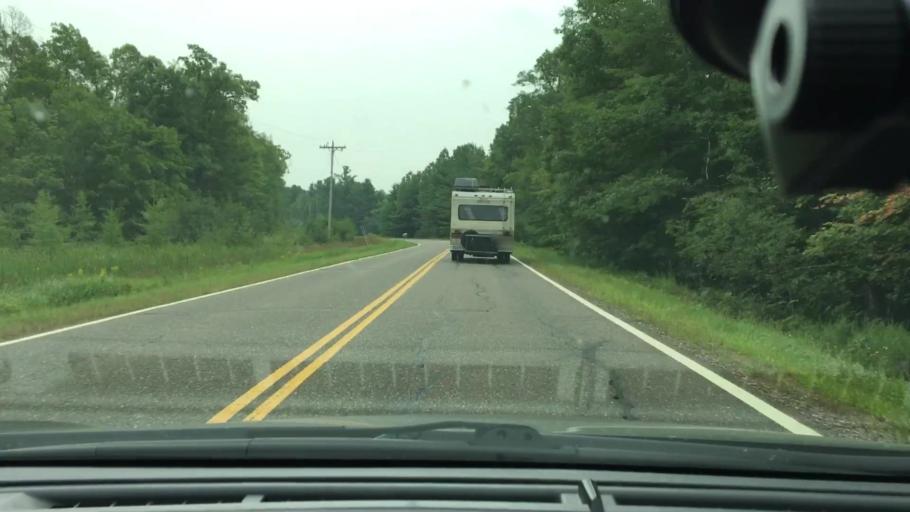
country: US
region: Minnesota
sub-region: Aitkin County
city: Aitkin
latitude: 46.4054
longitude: -93.8072
